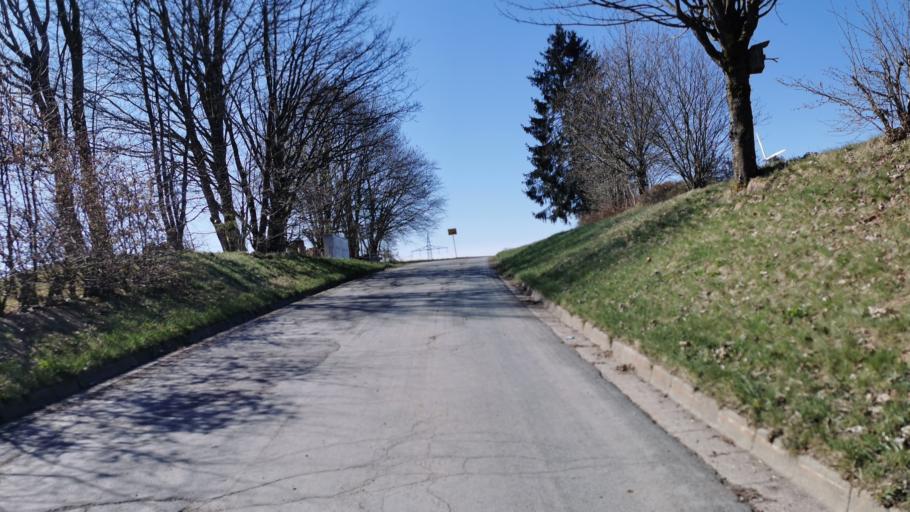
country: DE
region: Bavaria
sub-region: Upper Franconia
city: Teuschnitz
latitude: 50.4083
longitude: 11.3387
